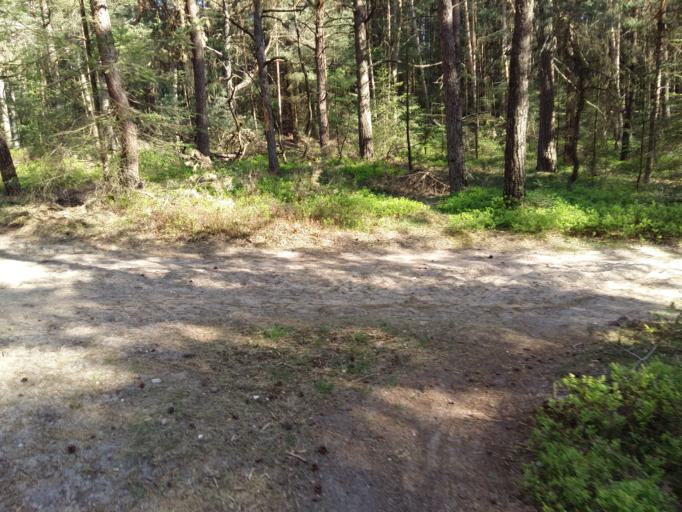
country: NL
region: Gelderland
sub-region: Gemeente Apeldoorn
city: Uddel
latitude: 52.3195
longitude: 5.7312
